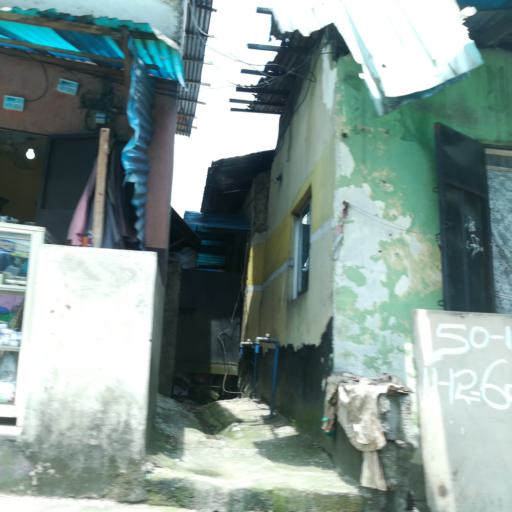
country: NG
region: Rivers
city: Port Harcourt
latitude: 4.7770
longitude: 7.0417
